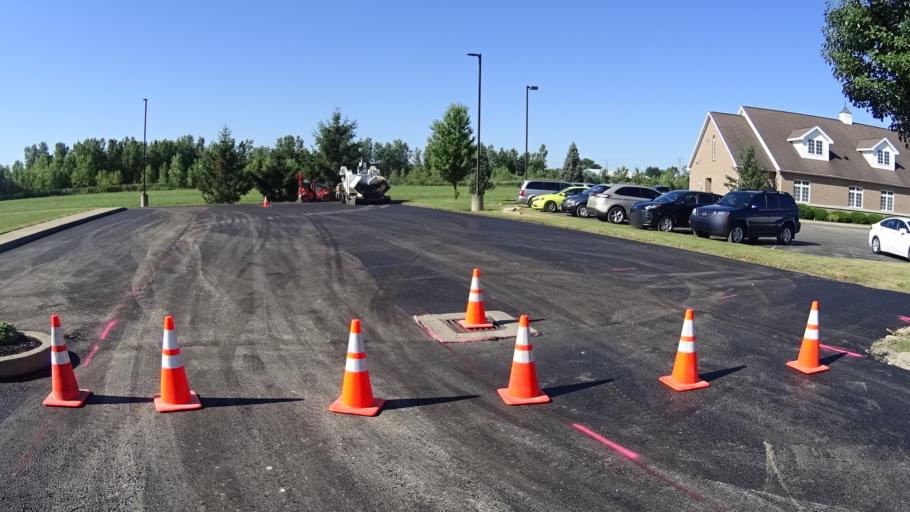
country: US
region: Ohio
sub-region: Erie County
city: Sandusky
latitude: 41.4263
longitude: -82.7150
